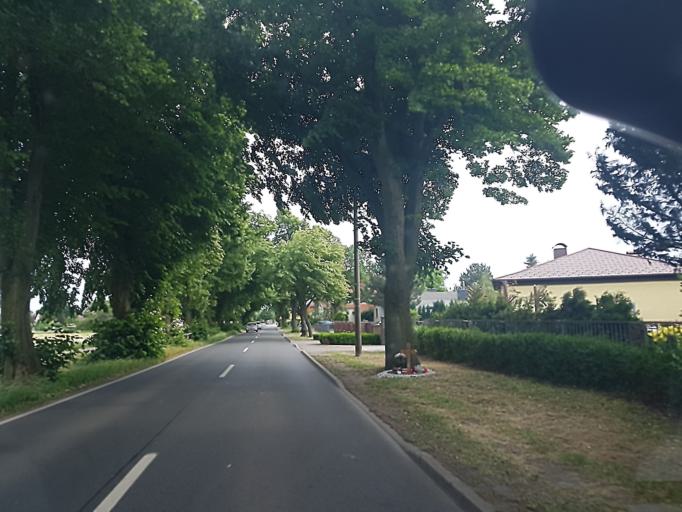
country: DE
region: Saxony-Anhalt
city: Wittenburg
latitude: 51.8808
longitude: 12.6302
